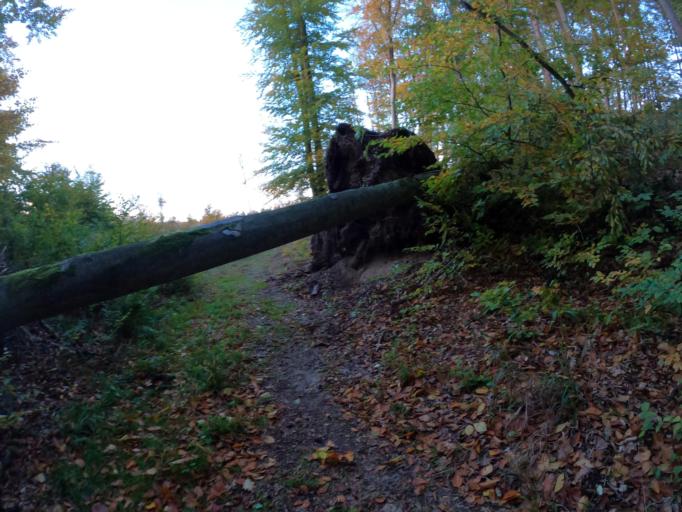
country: PL
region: West Pomeranian Voivodeship
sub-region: Powiat mysliborski
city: Barlinek
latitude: 52.9742
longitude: 15.2312
